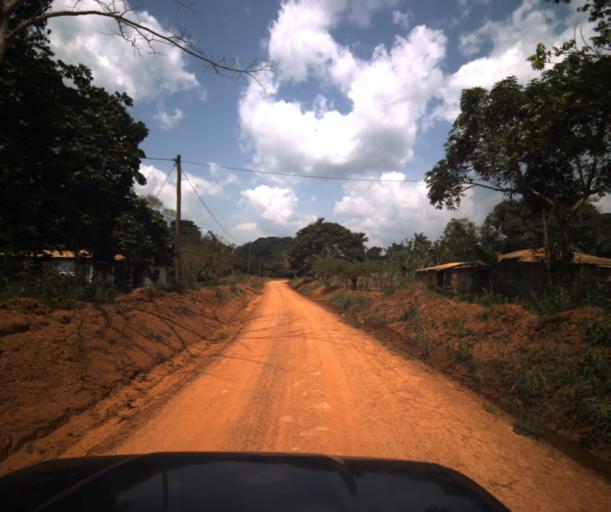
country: CM
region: Centre
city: Akono
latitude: 3.5580
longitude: 11.0687
